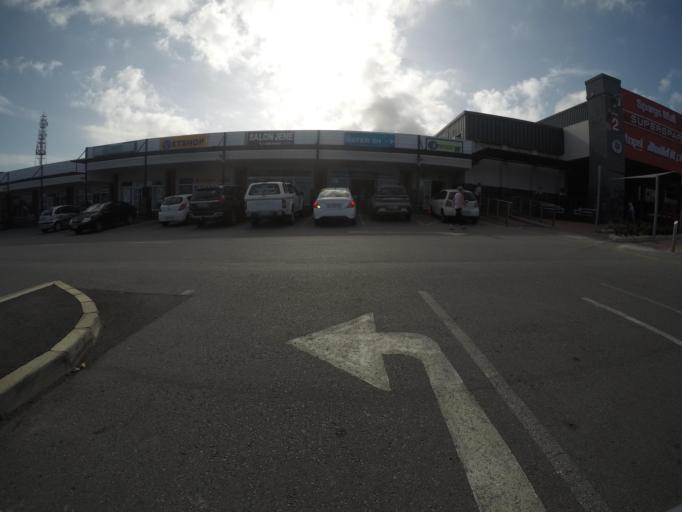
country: ZA
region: Eastern Cape
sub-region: Buffalo City Metropolitan Municipality
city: East London
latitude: -32.9682
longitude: 27.9404
